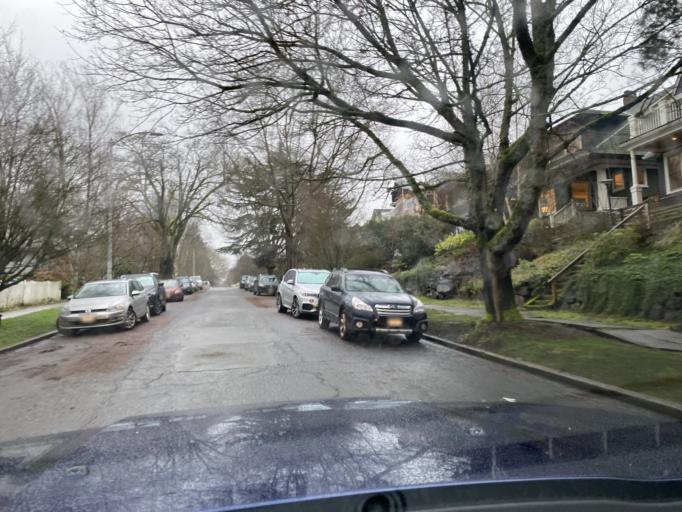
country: US
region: Washington
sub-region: King County
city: Seattle
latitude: 47.6316
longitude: -122.3100
